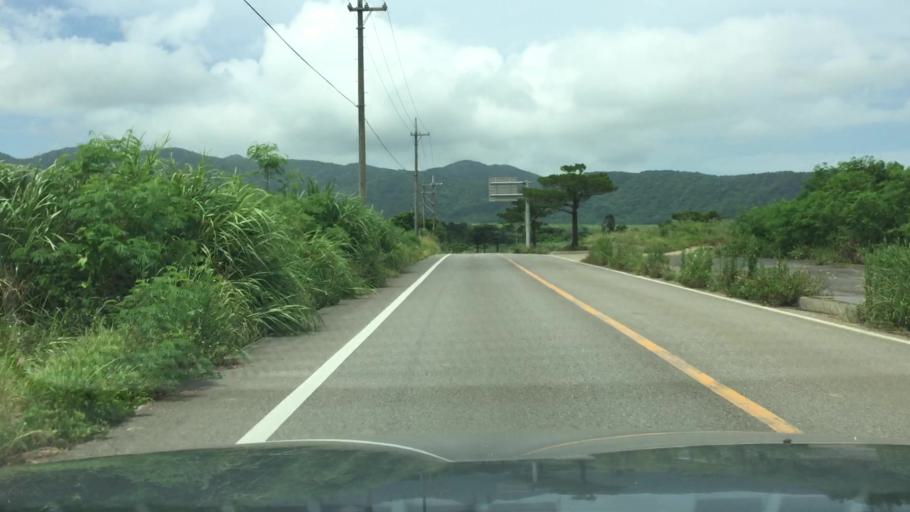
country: JP
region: Okinawa
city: Ishigaki
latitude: 24.4124
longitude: 124.2144
